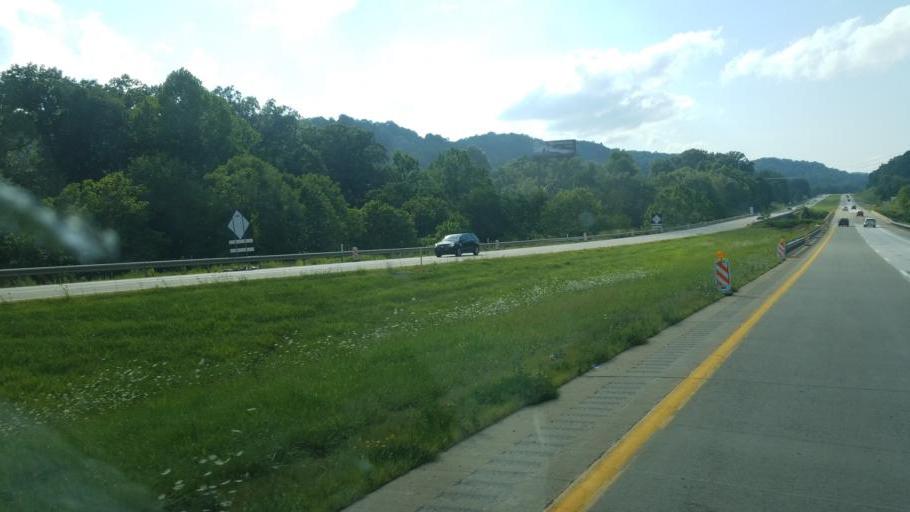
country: US
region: West Virginia
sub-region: Monongalia County
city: Star City
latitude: 39.7413
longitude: -80.0608
